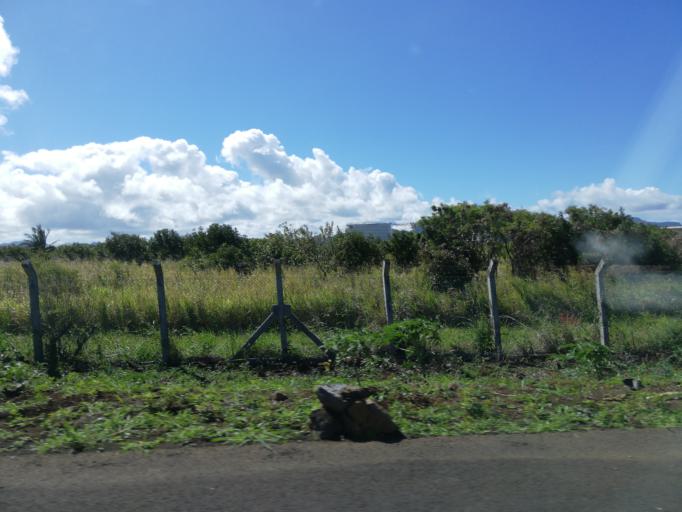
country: MU
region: Grand Port
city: Plaine Magnien
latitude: -20.4443
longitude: 57.6827
